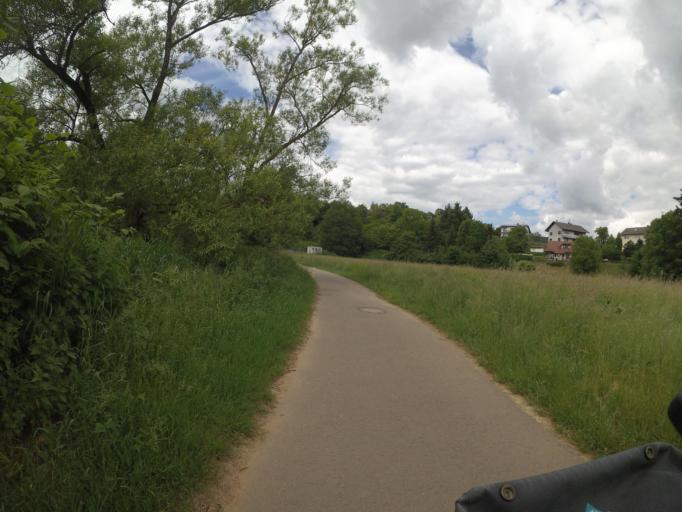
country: DE
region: Rheinland-Pfalz
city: Ulmet
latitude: 49.5878
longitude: 7.4542
